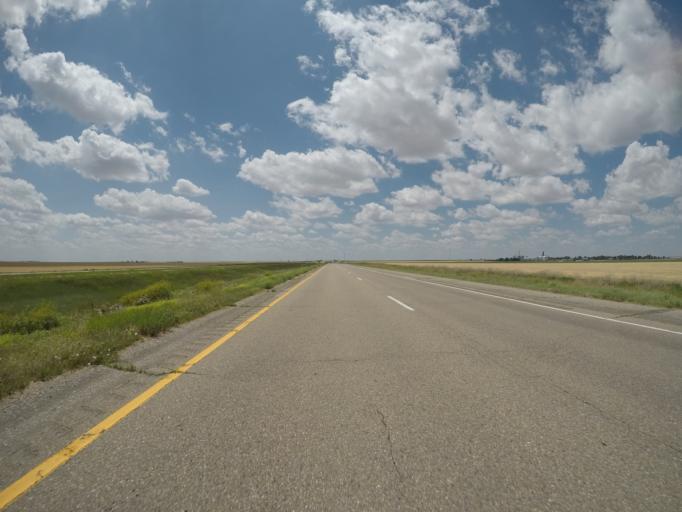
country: US
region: Colorado
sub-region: Kit Carson County
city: Burlington
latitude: 39.2942
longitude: -102.4106
